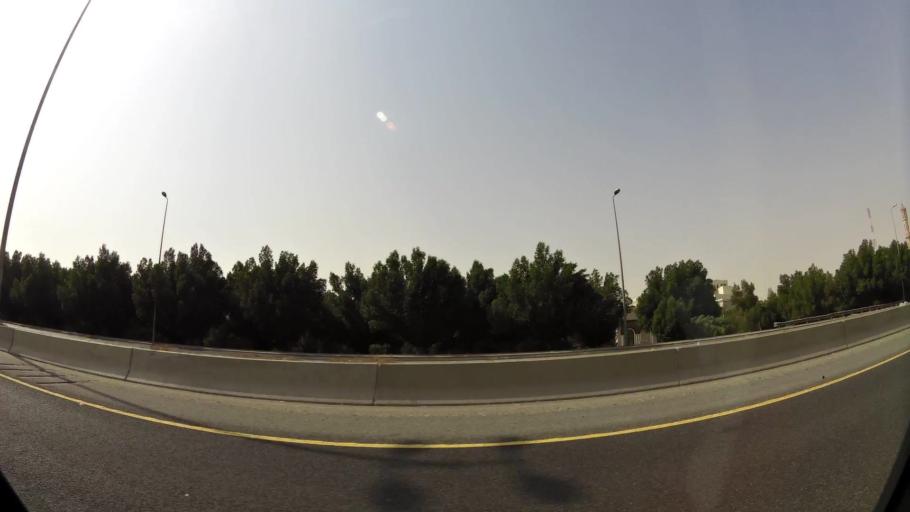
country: KW
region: Muhafazat al Jahra'
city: Al Jahra'
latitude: 29.3596
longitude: 47.6746
